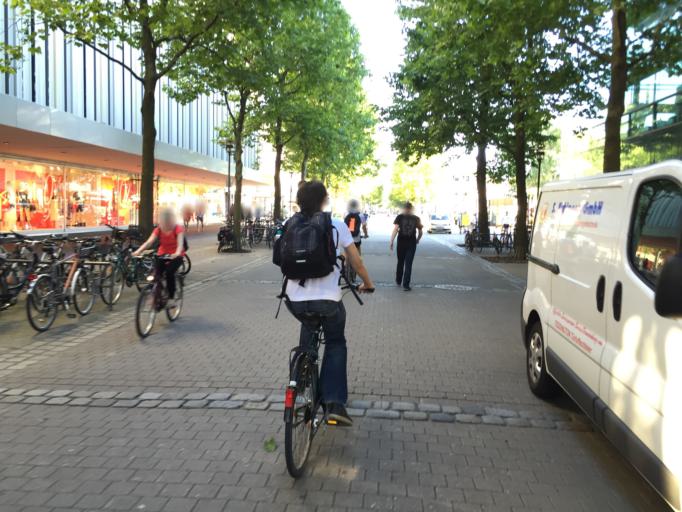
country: DE
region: Bavaria
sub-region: Regierungsbezirk Mittelfranken
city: Erlangen
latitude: 49.5924
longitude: 11.0057
